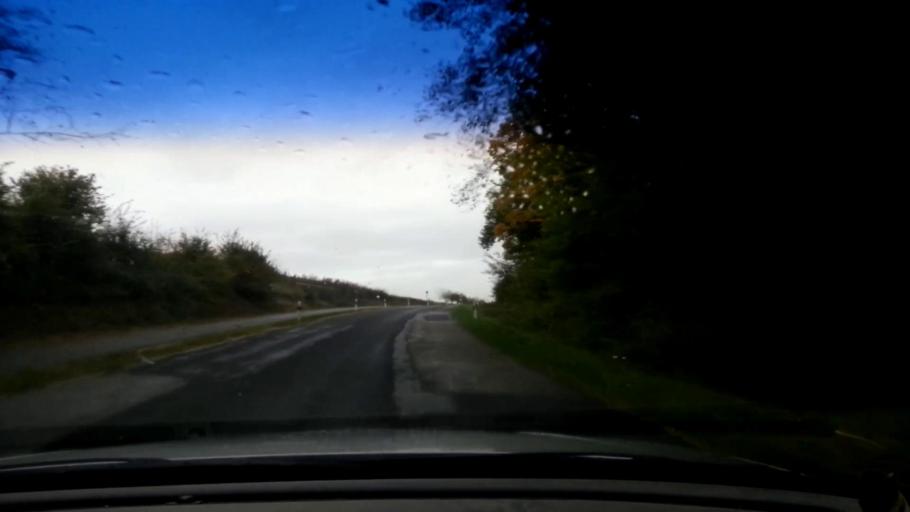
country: DE
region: Bavaria
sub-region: Upper Franconia
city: Priesendorf
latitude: 49.8742
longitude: 10.7079
